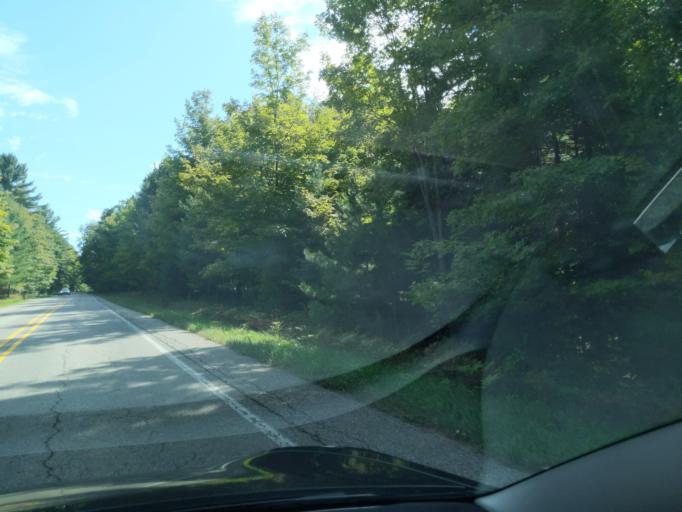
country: US
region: Michigan
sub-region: Antrim County
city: Bellaire
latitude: 45.0744
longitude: -85.3197
